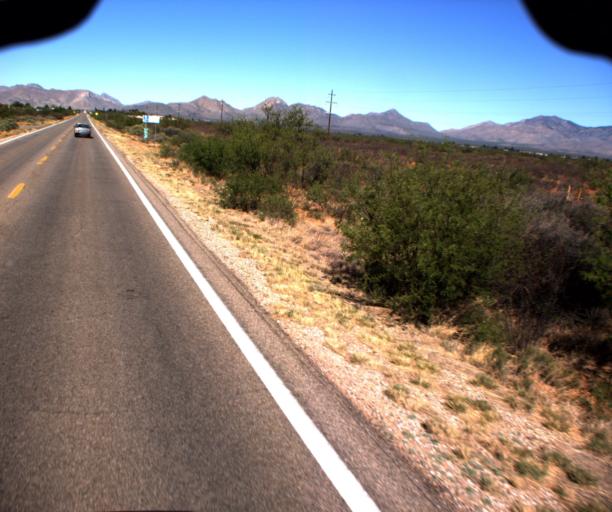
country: US
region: Arizona
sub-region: Cochise County
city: Huachuca City
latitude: 31.6933
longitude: -110.3256
